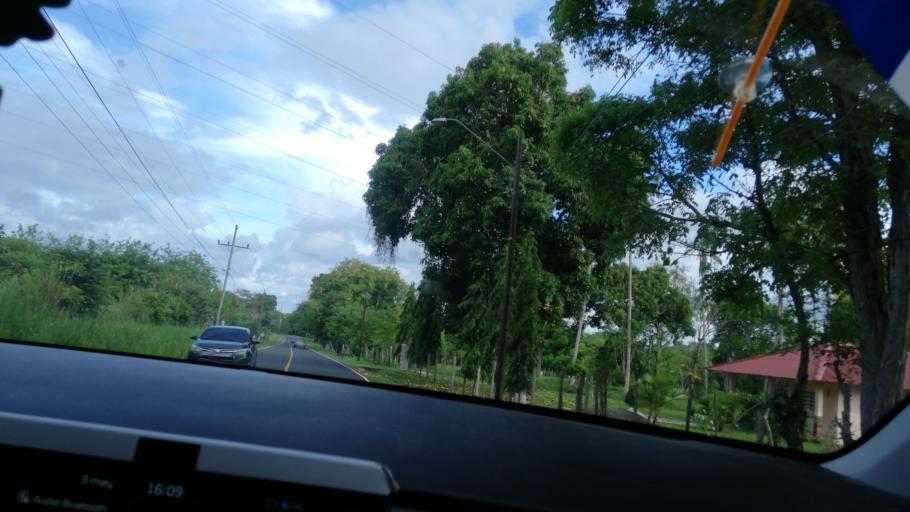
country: PA
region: Panama
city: Las Colinas
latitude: 8.4907
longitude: -80.0231
